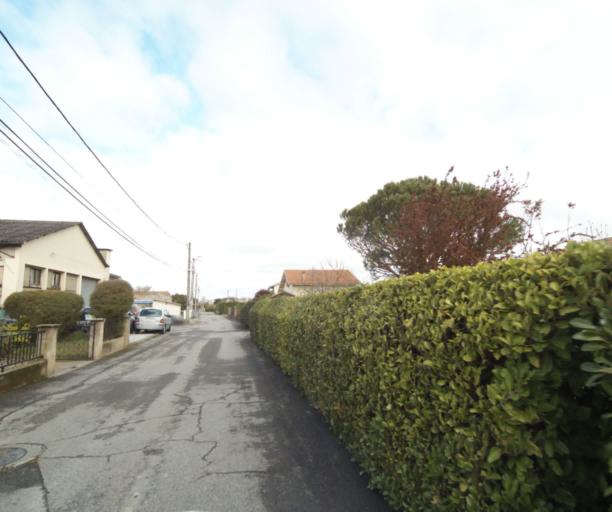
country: FR
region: Midi-Pyrenees
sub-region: Departement de l'Ariege
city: Saverdun
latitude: 43.2406
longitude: 1.5704
